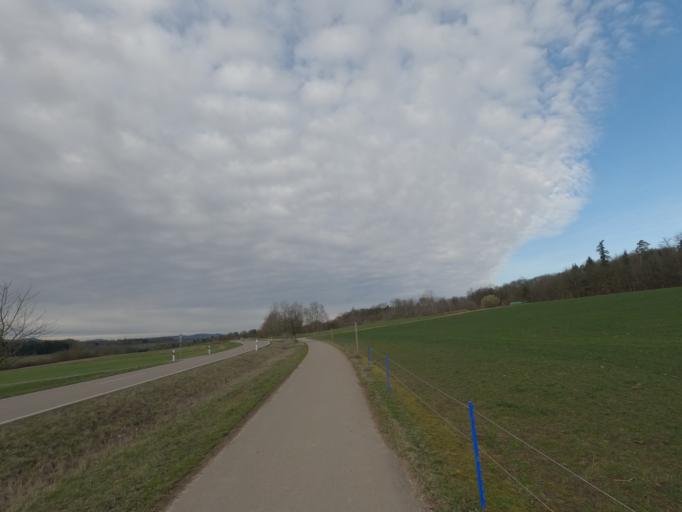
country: DE
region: Baden-Wuerttemberg
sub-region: Regierungsbezirk Stuttgart
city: Zell unter Aichelberg
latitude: 48.6528
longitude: 9.5598
